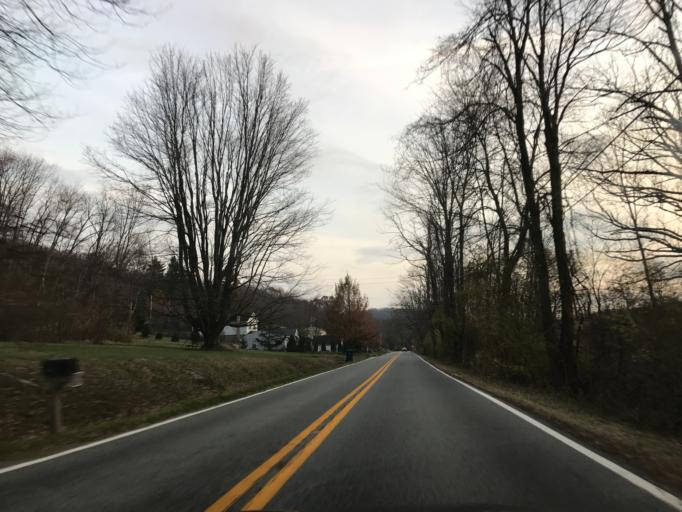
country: US
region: Maryland
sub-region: Frederick County
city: Braddock Heights
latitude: 39.4494
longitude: -77.4954
